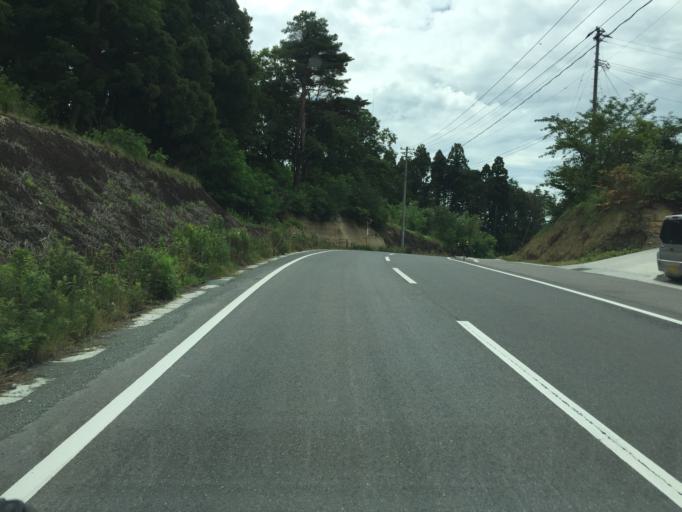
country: JP
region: Miyagi
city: Marumori
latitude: 37.8151
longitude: 140.9522
